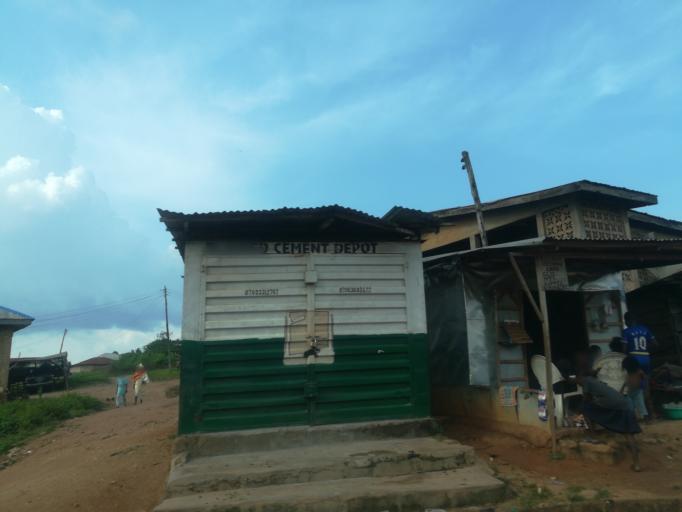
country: NG
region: Oyo
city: Moniya
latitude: 7.5260
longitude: 3.9263
